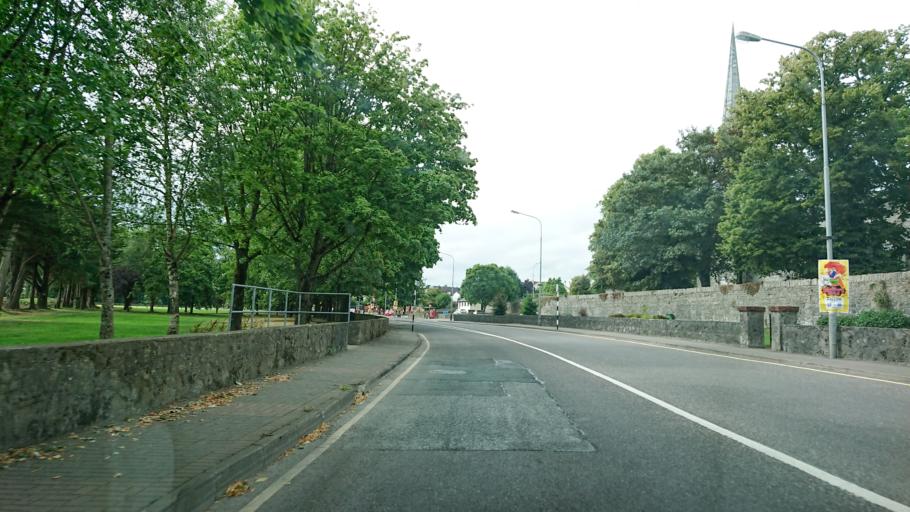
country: IE
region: Munster
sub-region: County Cork
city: Mallow
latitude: 52.1349
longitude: -8.6431
